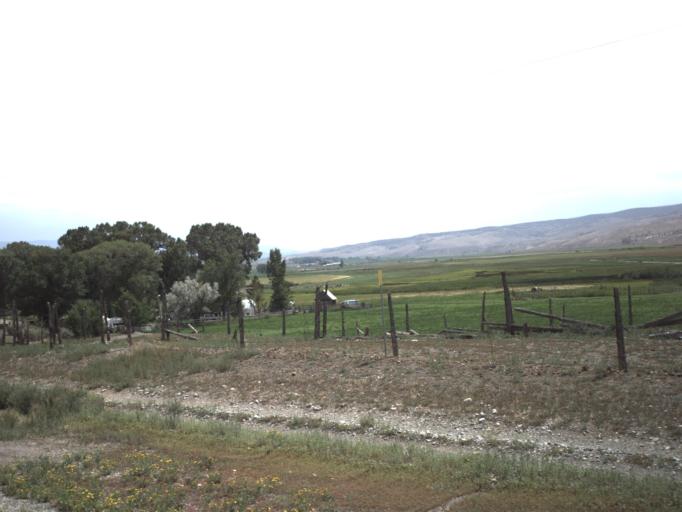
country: US
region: Utah
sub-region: Piute County
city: Junction
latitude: 38.1608
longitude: -112.0092
